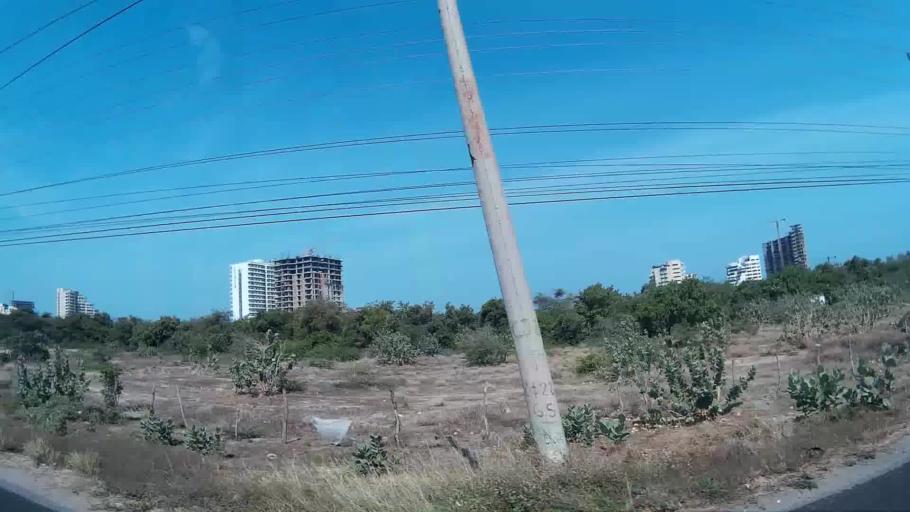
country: CO
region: Magdalena
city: Santa Marta
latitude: 11.1522
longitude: -74.2223
